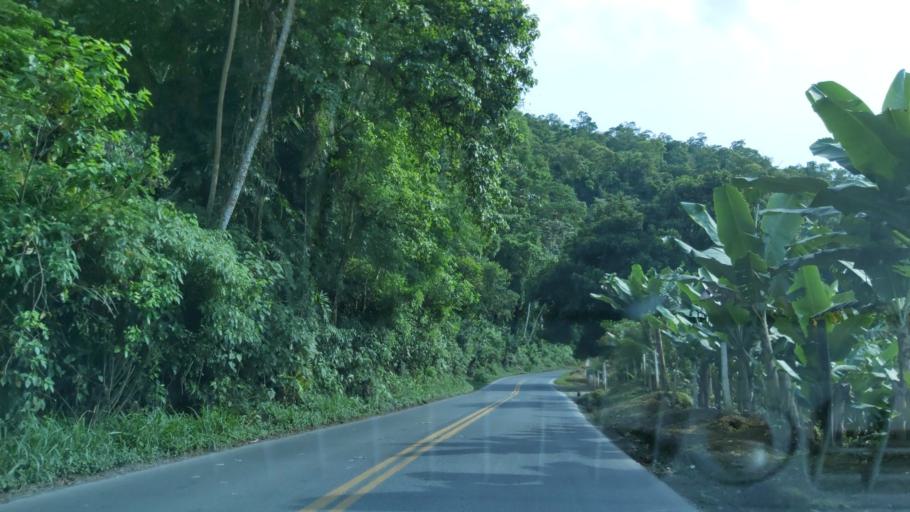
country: BR
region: Sao Paulo
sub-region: Juquia
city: Juquia
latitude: -24.0857
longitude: -47.6124
